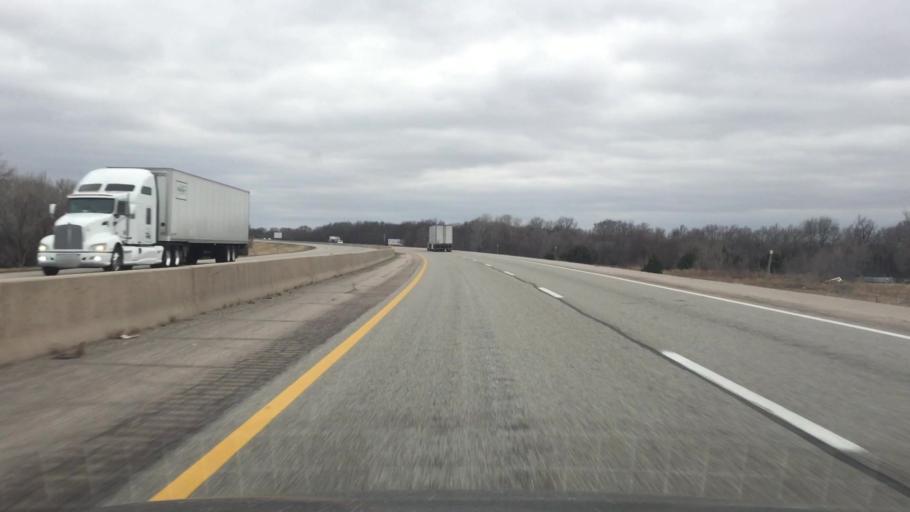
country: US
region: Kansas
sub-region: Butler County
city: El Dorado
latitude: 37.8684
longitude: -96.8566
